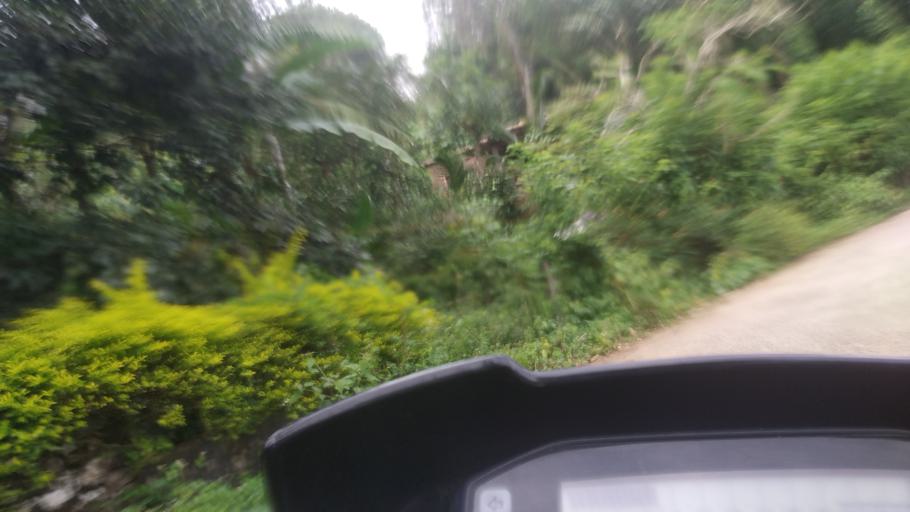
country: IN
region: Tamil Nadu
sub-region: Theni
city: Gudalur
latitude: 9.5768
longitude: 77.0773
